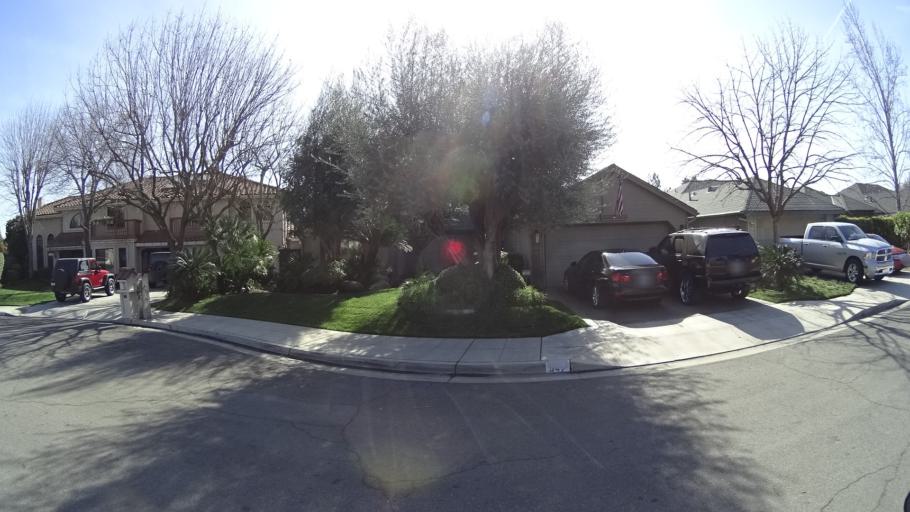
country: US
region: California
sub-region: Fresno County
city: Clovis
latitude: 36.8839
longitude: -119.7727
